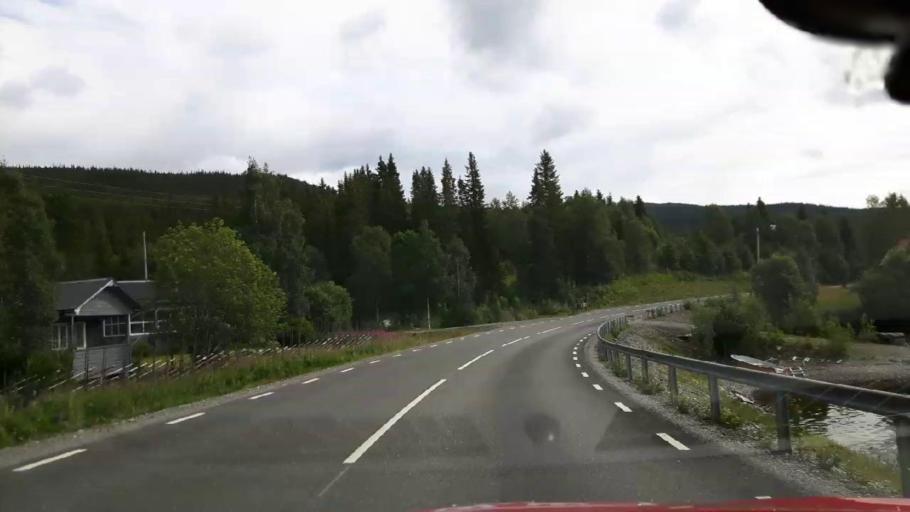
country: NO
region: Nord-Trondelag
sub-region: Lierne
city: Sandvika
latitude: 64.6509
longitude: 14.1368
